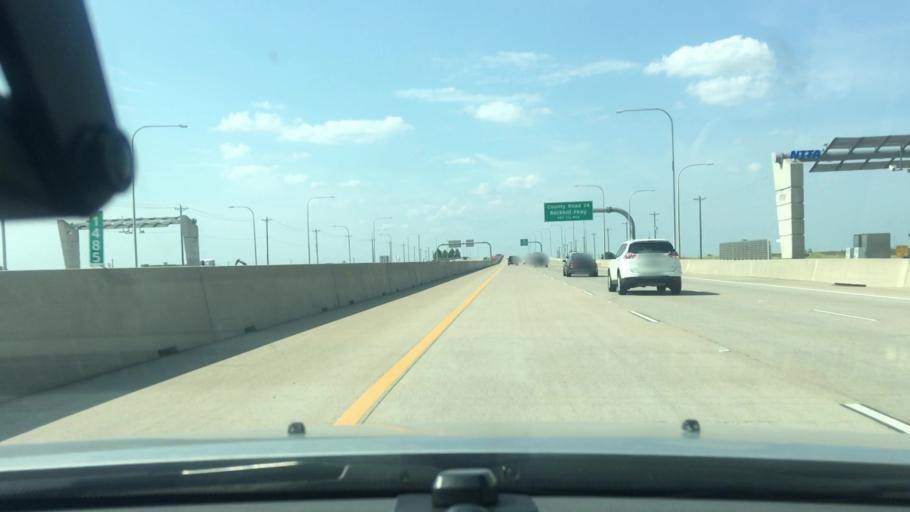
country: US
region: Texas
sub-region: Collin County
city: Frisco
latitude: 33.1839
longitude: -96.8392
